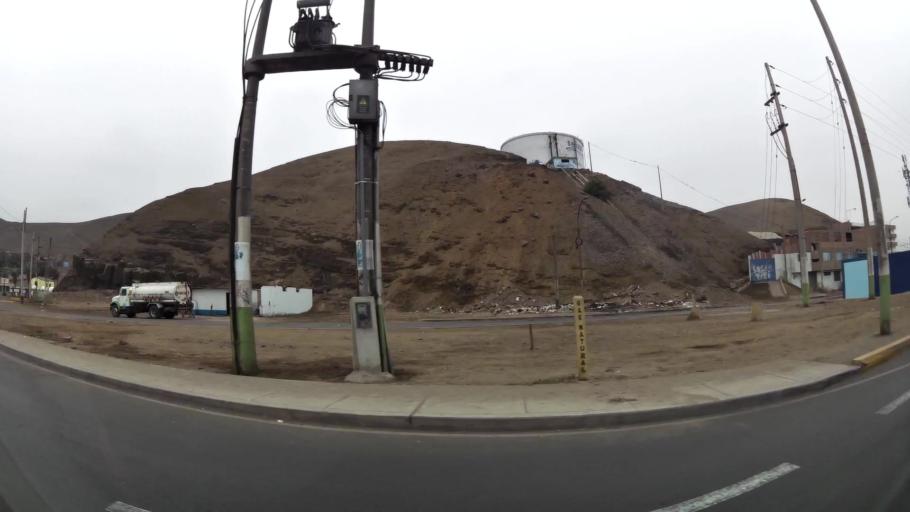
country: PE
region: Lima
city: Ventanilla
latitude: -11.9424
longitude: -77.1313
